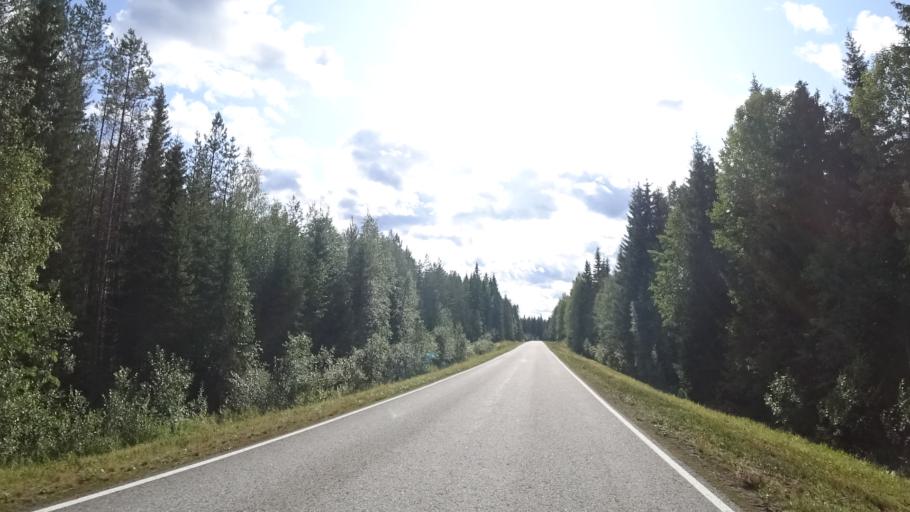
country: RU
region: Republic of Karelia
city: Vyartsilya
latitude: 62.2405
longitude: 30.7041
